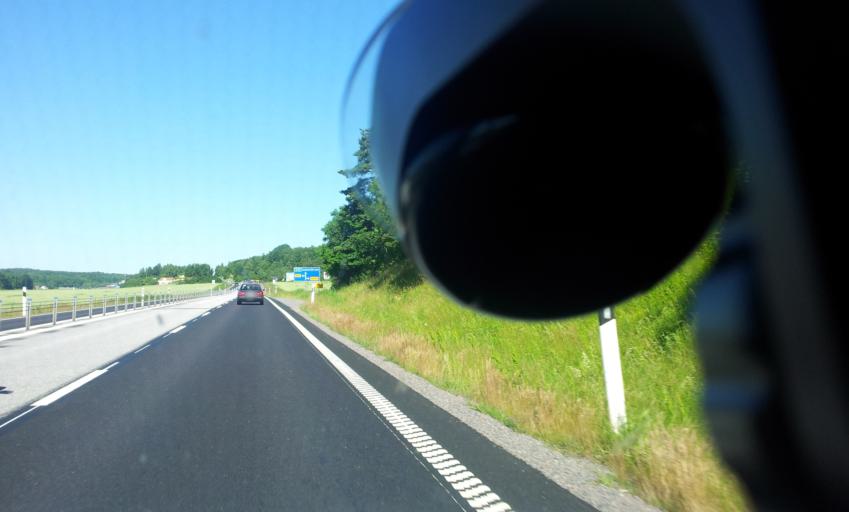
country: SE
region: OEstergoetland
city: Lindo
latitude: 58.5484
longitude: 16.2575
